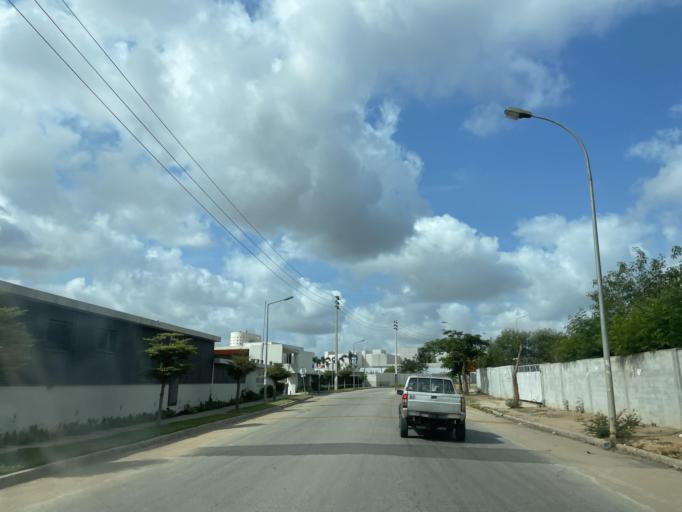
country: AO
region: Luanda
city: Luanda
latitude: -8.9302
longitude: 13.1906
